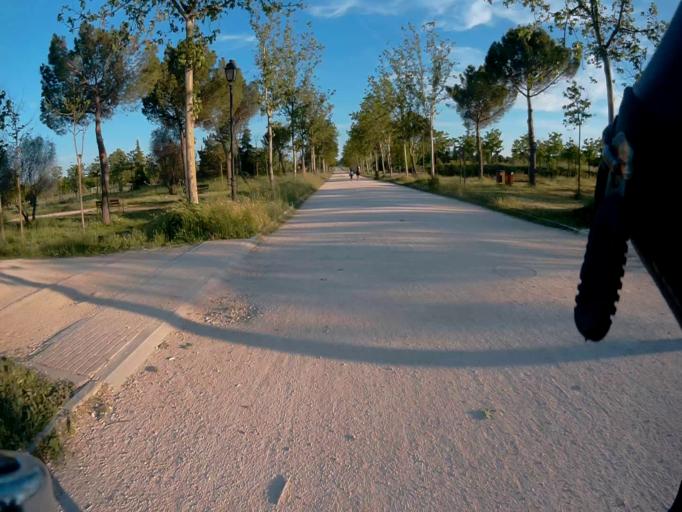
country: ES
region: Madrid
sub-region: Provincia de Madrid
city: Alcorcon
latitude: 40.3243
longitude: -3.8004
